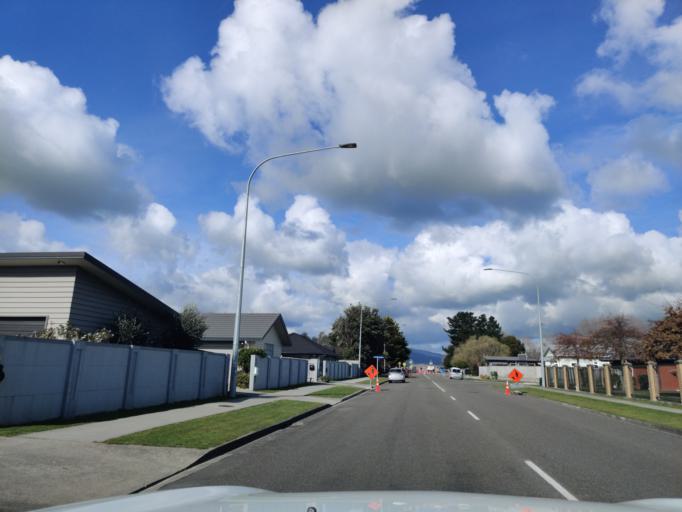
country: NZ
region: Manawatu-Wanganui
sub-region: Palmerston North City
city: Palmerston North
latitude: -40.3269
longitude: 175.6631
